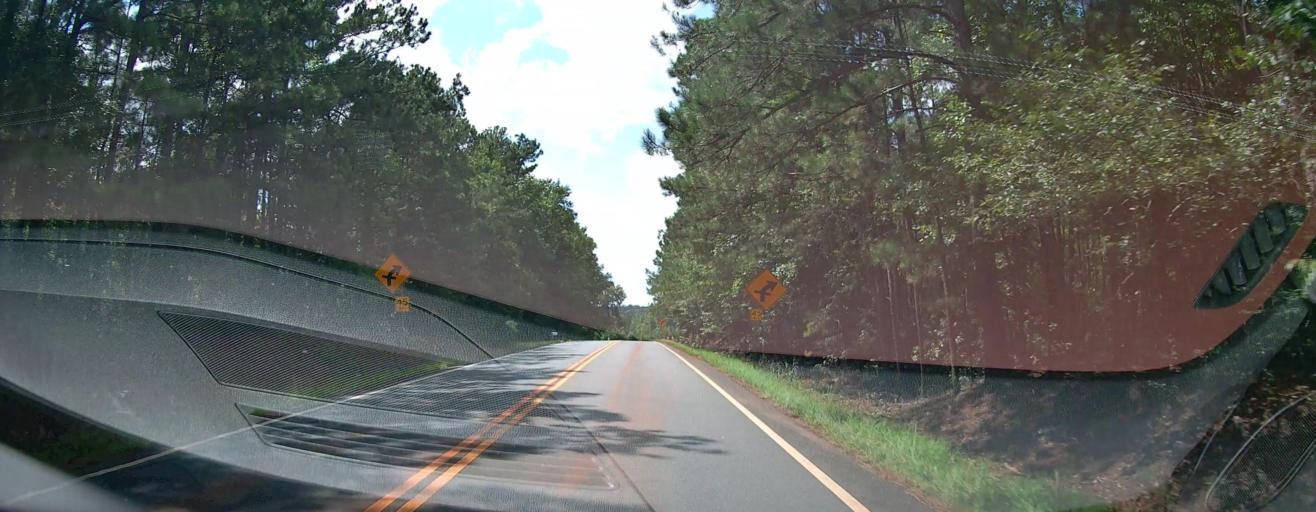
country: US
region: Georgia
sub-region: Crawford County
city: Knoxville
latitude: 32.8746
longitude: -83.9921
